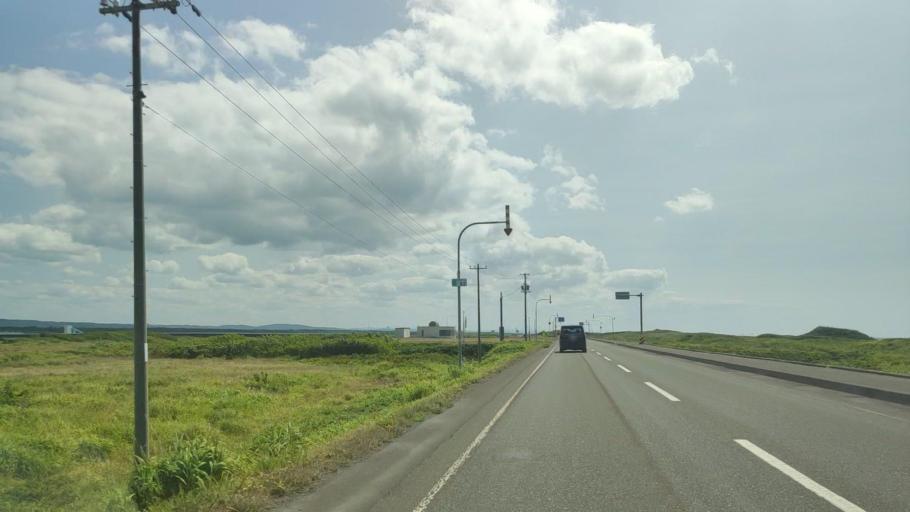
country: JP
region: Hokkaido
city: Makubetsu
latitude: 44.9272
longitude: 141.7212
